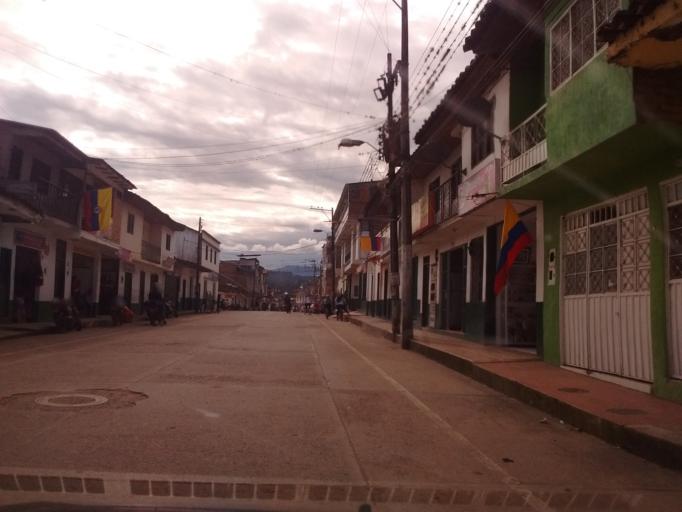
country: CO
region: Huila
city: San Agustin
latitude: 1.8801
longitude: -76.2692
